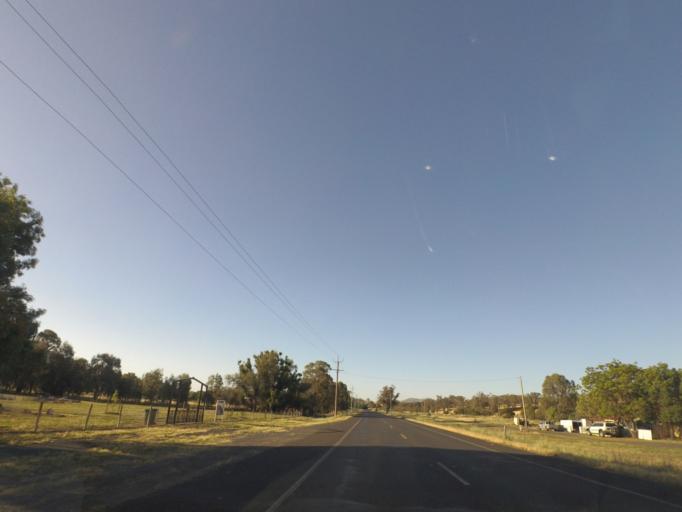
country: AU
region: New South Wales
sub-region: Gundagai
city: Gundagai
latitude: -34.9319
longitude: 148.1667
